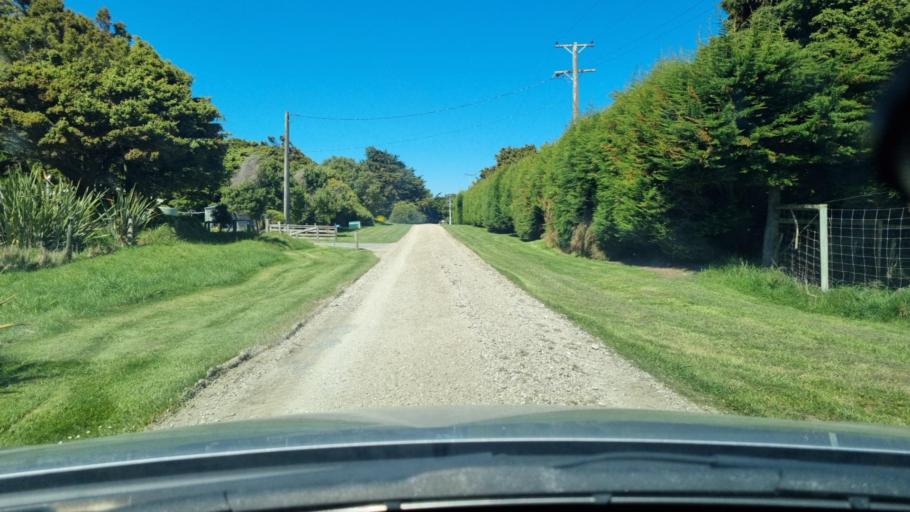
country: NZ
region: Southland
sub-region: Invercargill City
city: Invercargill
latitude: -46.4555
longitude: 168.2813
